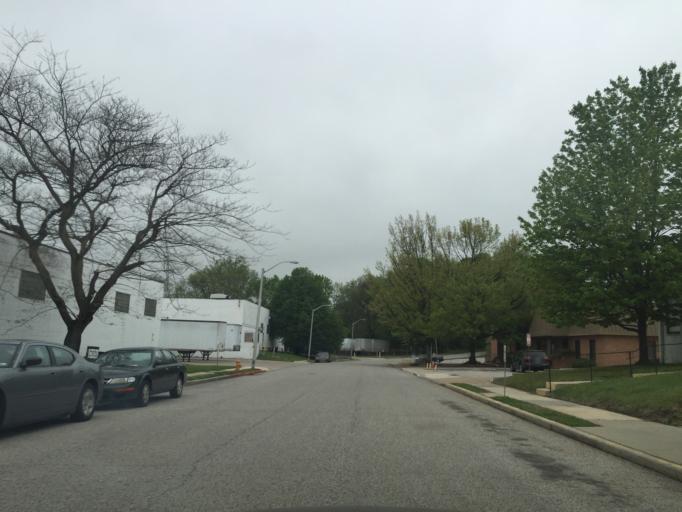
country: US
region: Maryland
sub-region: City of Baltimore
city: Baltimore
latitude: 39.3391
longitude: -76.6456
